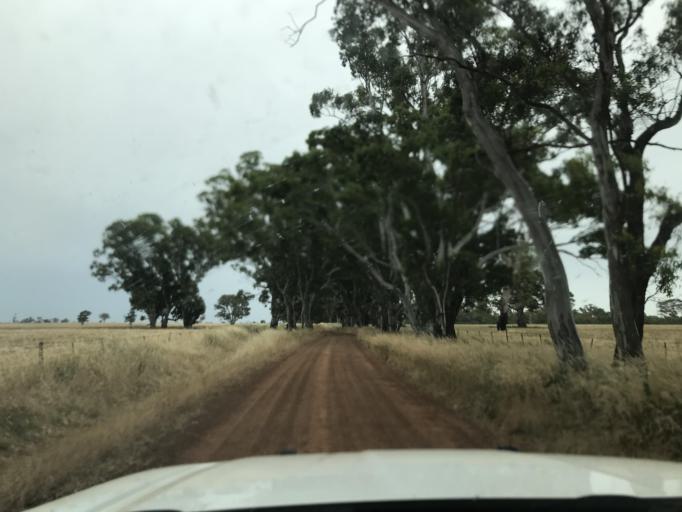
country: AU
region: Victoria
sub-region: Horsham
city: Horsham
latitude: -37.0655
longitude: 141.6607
